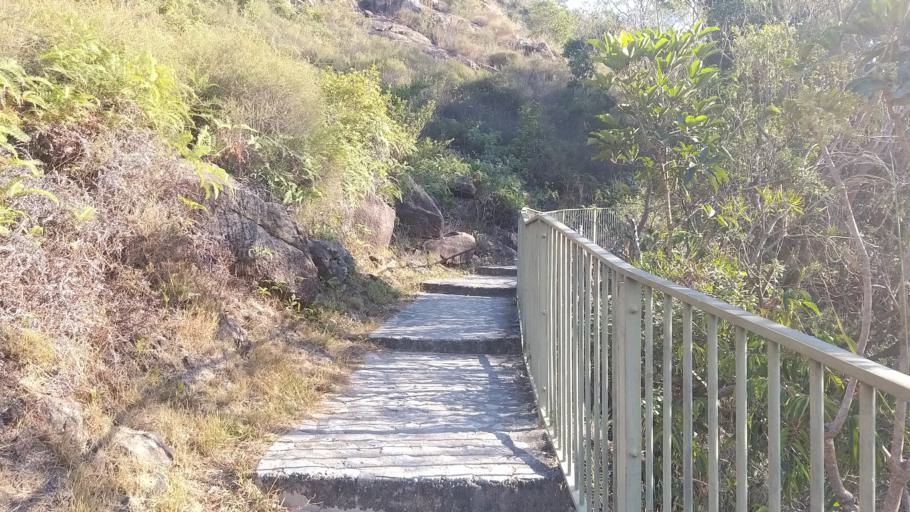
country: HK
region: Tuen Mun
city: Tuen Mun
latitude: 22.3983
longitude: 113.9836
